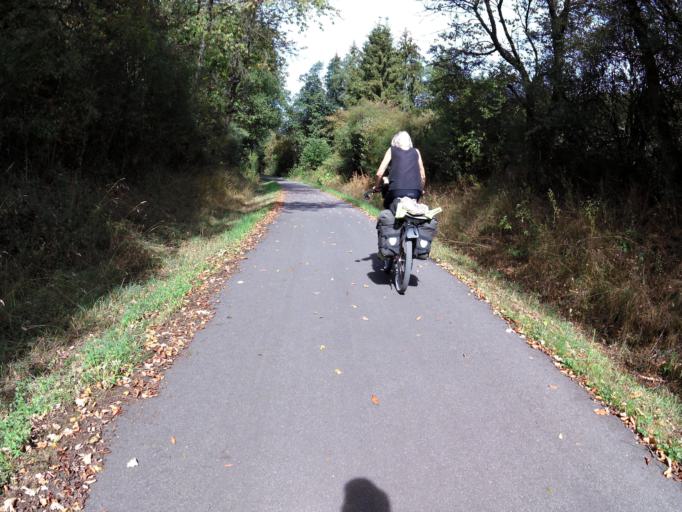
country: DE
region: Rheinland-Pfalz
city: Kickeshausen
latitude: 50.0587
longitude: 6.2486
